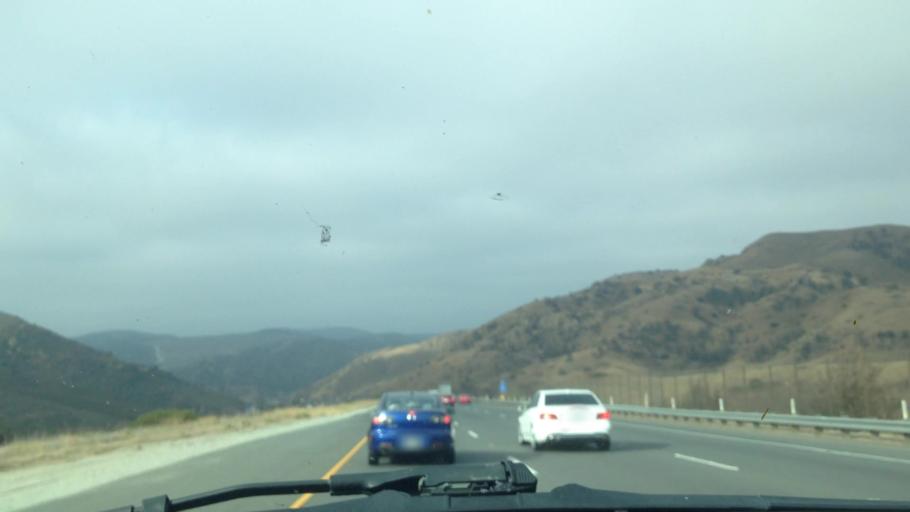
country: US
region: California
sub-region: Orange County
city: North Tustin
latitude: 33.8129
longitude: -117.7205
